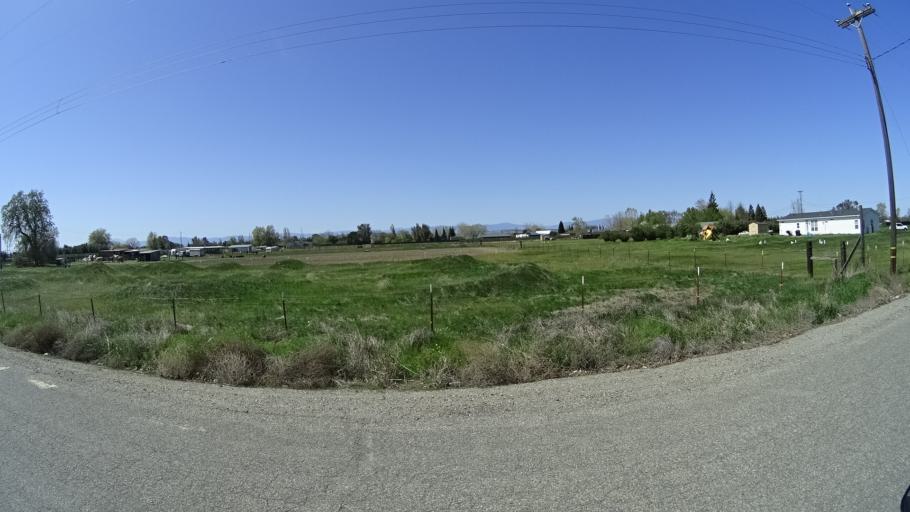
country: US
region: California
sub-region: Glenn County
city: Orland
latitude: 39.7632
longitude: -122.2296
